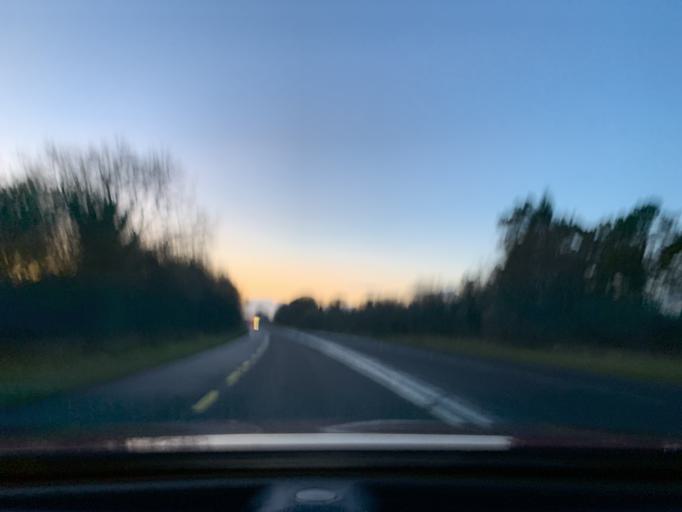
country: IE
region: Connaught
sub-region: County Leitrim
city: Carrick-on-Shannon
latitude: 53.9578
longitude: -8.1660
